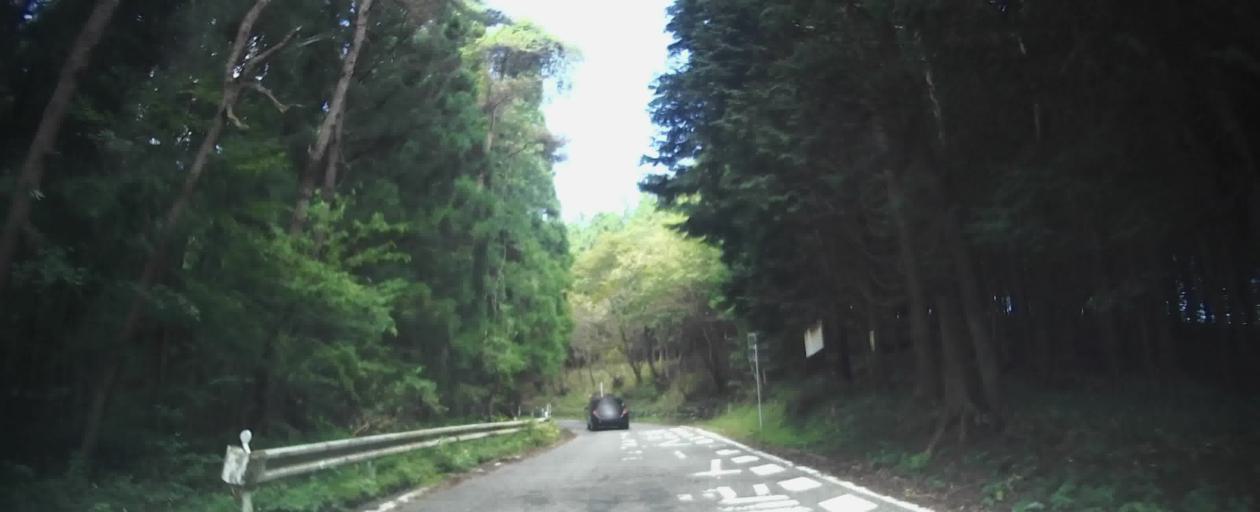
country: JP
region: Gunma
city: Shibukawa
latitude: 36.4596
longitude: 138.8942
